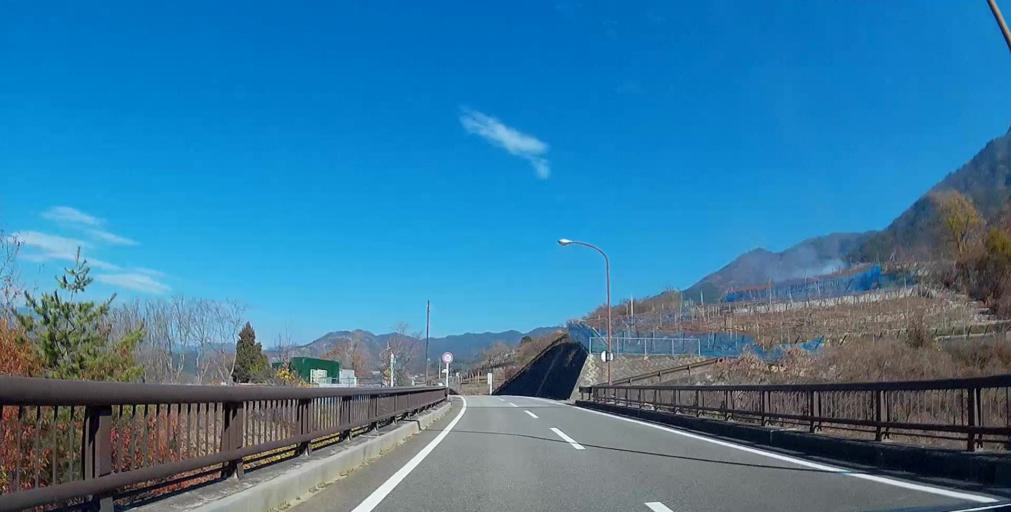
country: JP
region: Yamanashi
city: Enzan
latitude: 35.6702
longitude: 138.7451
